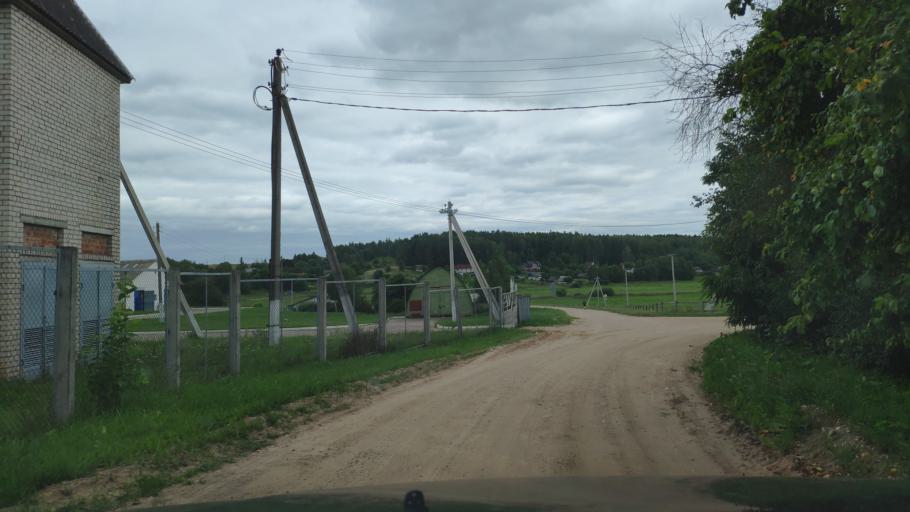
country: BY
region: Minsk
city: Khatsyezhyna
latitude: 53.9312
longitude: 27.2668
